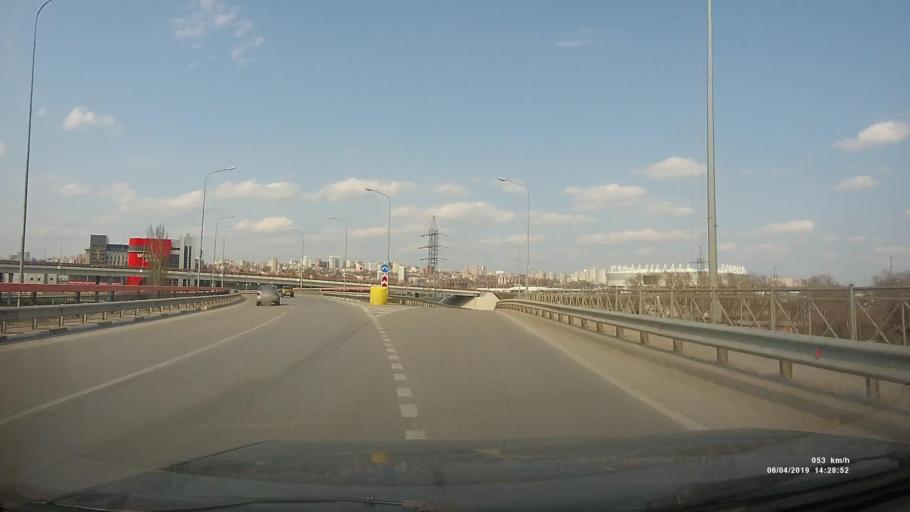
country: RU
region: Rostov
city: Rostov-na-Donu
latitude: 47.2032
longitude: 39.7292
